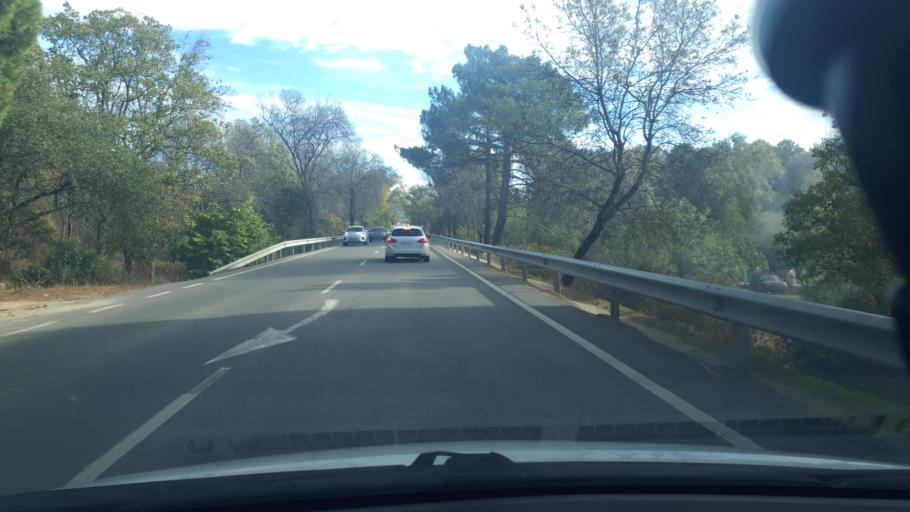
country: ES
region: Castille and Leon
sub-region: Provincia de Avila
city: La Adrada
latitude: 40.3080
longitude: -4.6515
